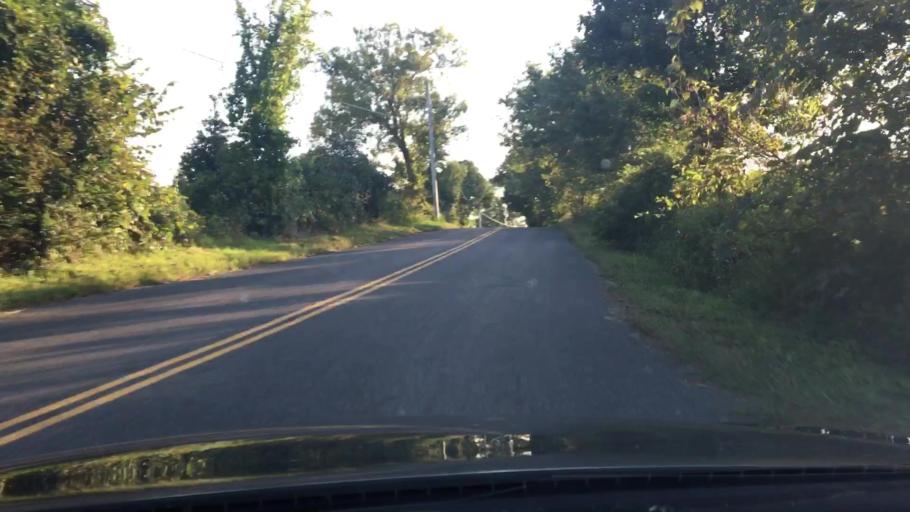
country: US
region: Connecticut
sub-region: Litchfield County
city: New Milford
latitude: 41.6026
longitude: -73.3705
